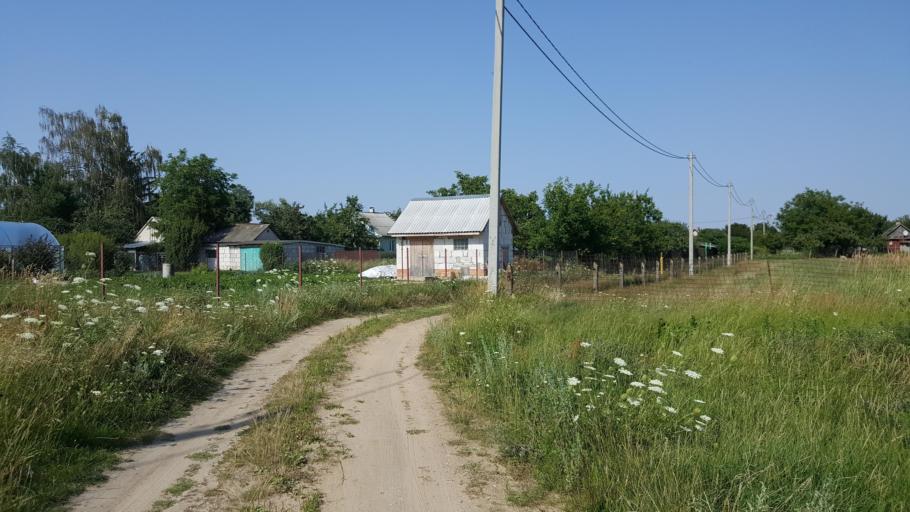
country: BY
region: Brest
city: Zhabinka
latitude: 52.2268
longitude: 23.9902
